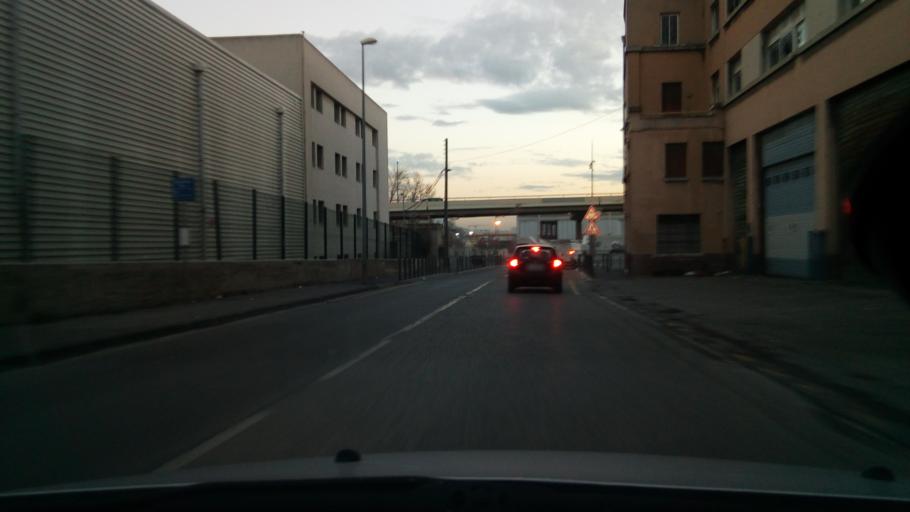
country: FR
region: Provence-Alpes-Cote d'Azur
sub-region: Departement des Bouches-du-Rhone
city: Marseille 14
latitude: 43.3303
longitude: 5.3665
